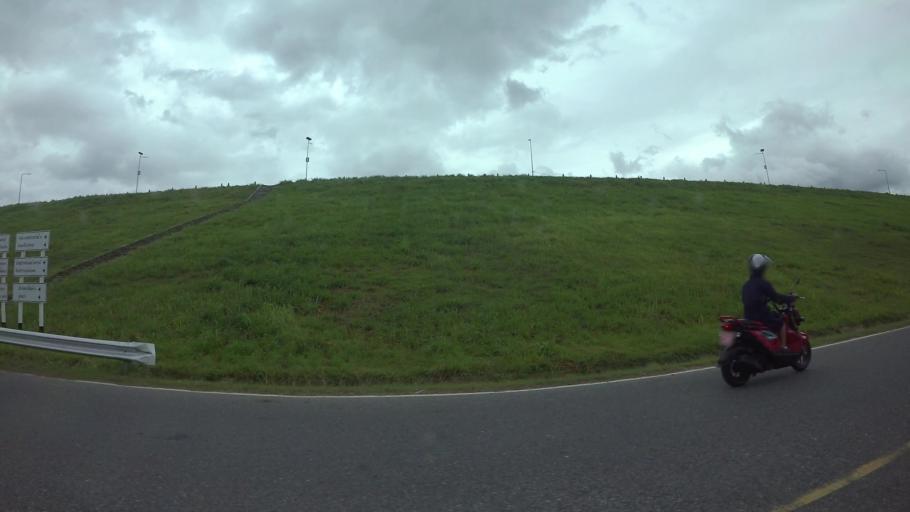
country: TH
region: Chon Buri
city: Si Racha
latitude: 13.2170
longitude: 100.9632
